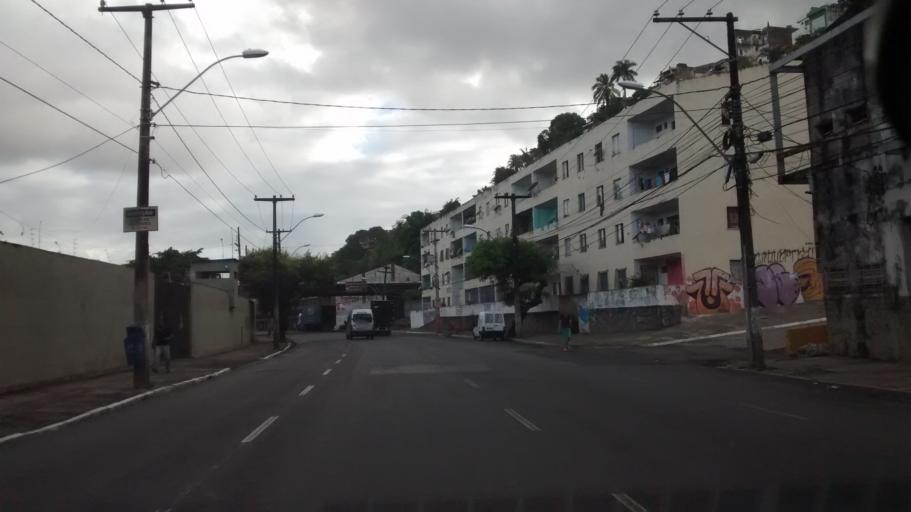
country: BR
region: Bahia
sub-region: Salvador
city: Salvador
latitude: -12.9652
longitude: -38.5067
